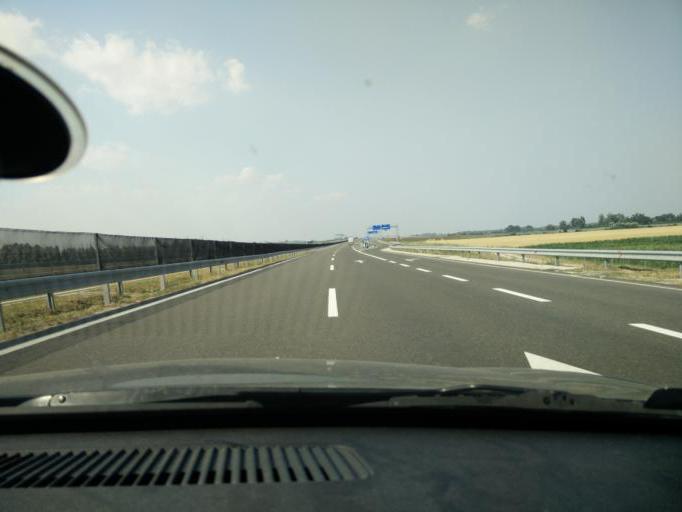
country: HU
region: Tolna
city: Szekszard
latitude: 46.3739
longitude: 18.7516
